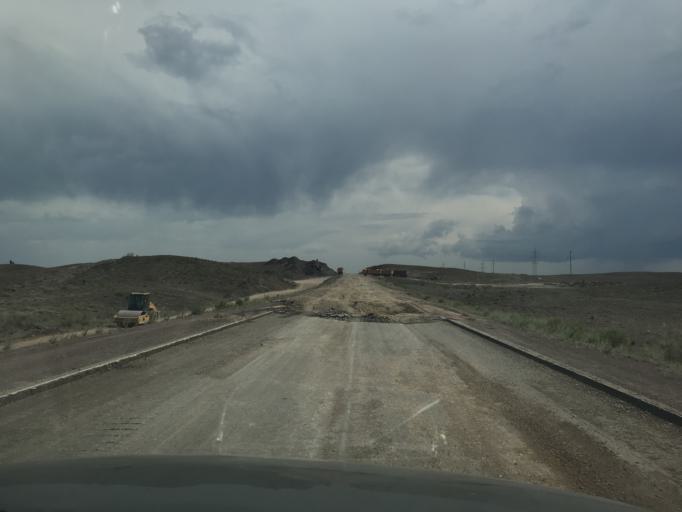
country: KZ
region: Zhambyl
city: Mynaral
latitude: 45.2841
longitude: 73.7754
